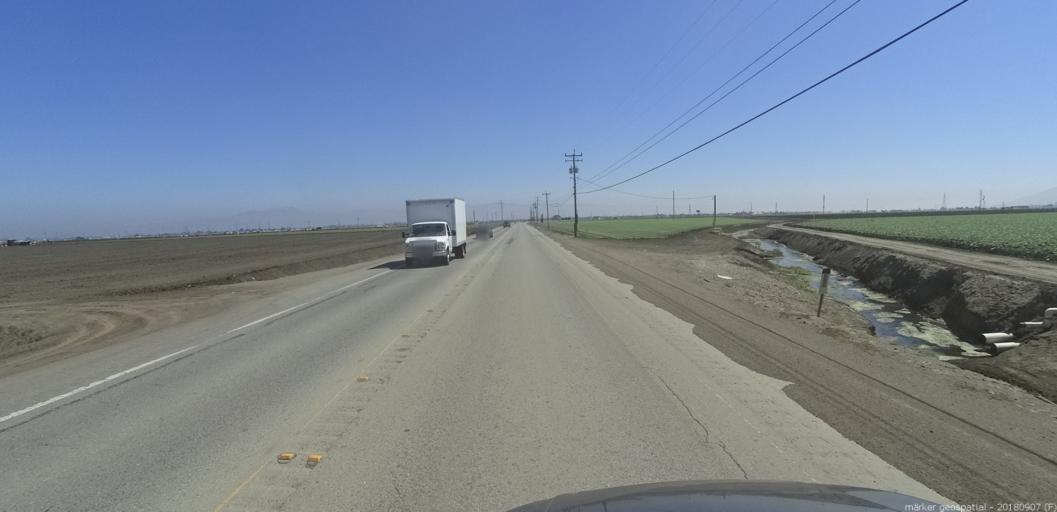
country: US
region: California
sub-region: Monterey County
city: Boronda
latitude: 36.6787
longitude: -121.7138
